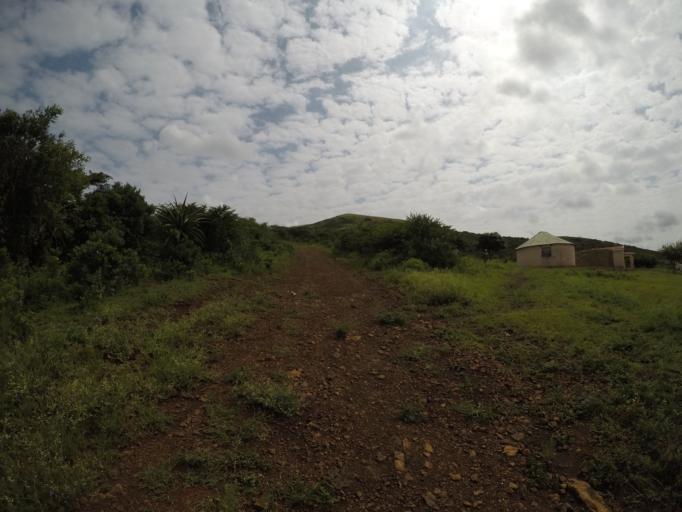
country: ZA
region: KwaZulu-Natal
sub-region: uThungulu District Municipality
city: Empangeni
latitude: -28.6127
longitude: 31.9049
